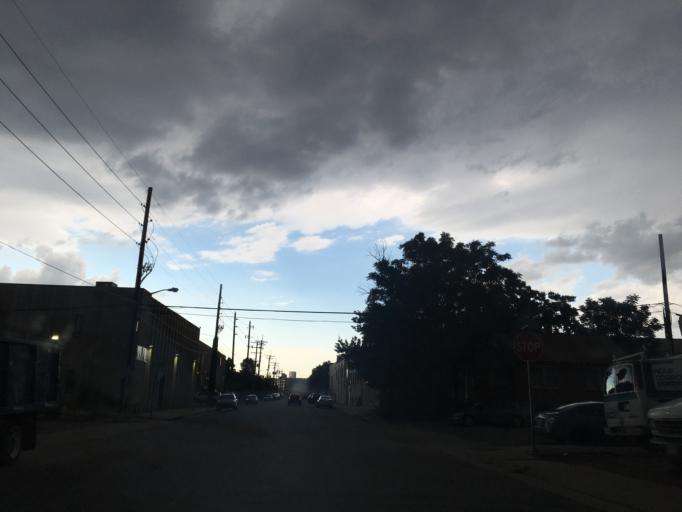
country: US
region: Colorado
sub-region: Arapahoe County
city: Englewood
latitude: 39.6891
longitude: -104.9887
